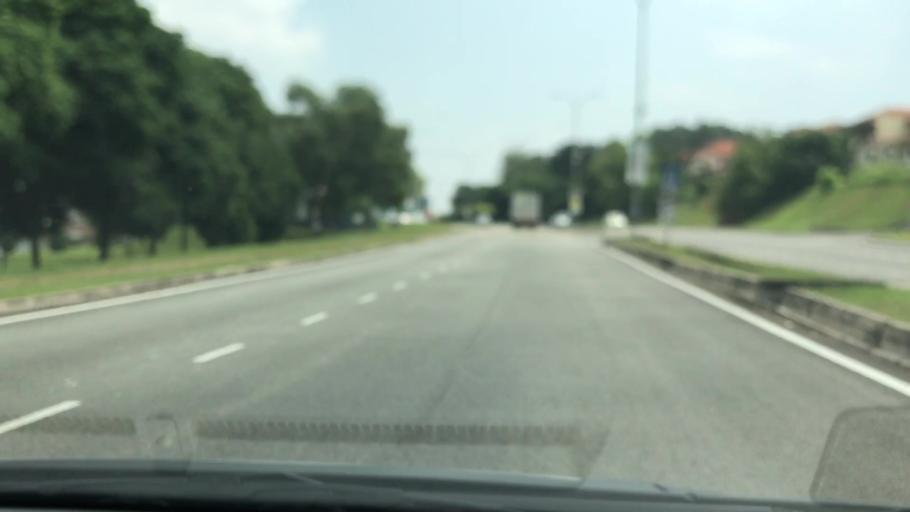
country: MY
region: Putrajaya
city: Putrajaya
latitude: 2.9877
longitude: 101.6643
